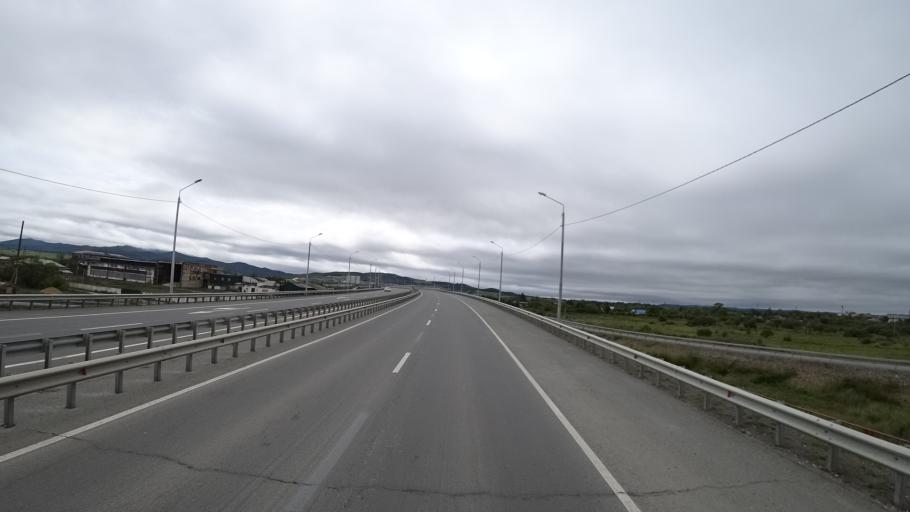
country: RU
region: Primorskiy
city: Monastyrishche
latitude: 44.1947
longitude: 132.4435
